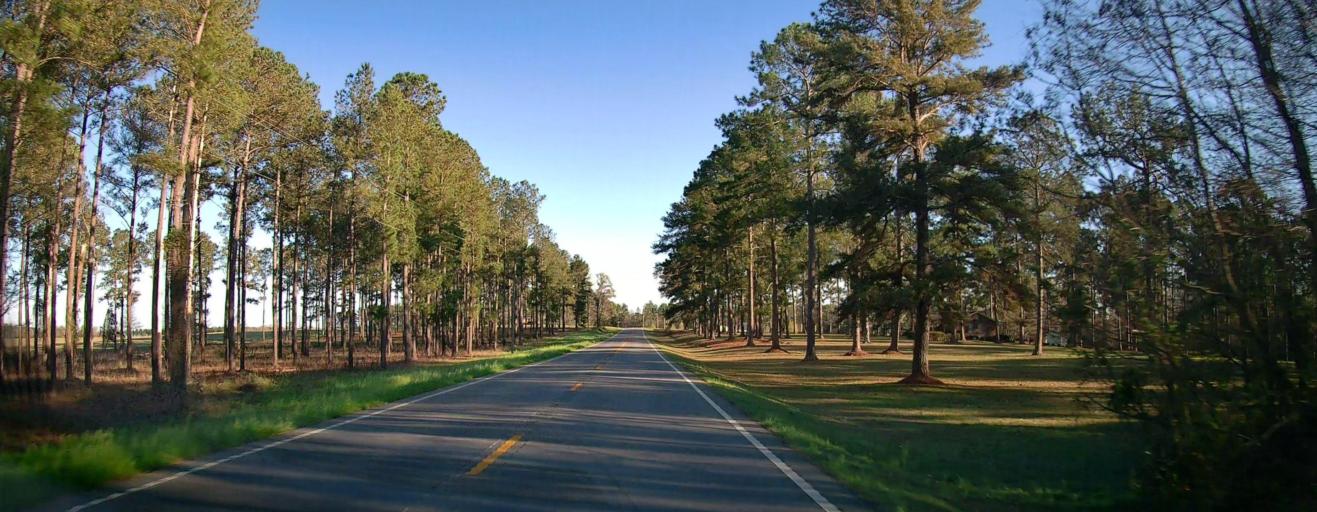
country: US
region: Georgia
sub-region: Pulaski County
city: Hawkinsville
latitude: 32.2143
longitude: -83.3834
